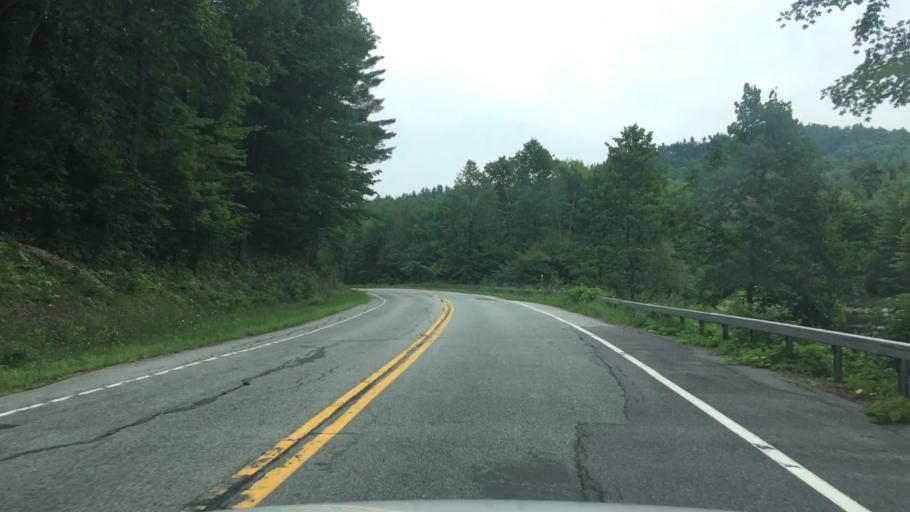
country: US
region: New York
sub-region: Essex County
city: Keeseville
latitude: 44.4250
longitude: -73.6803
